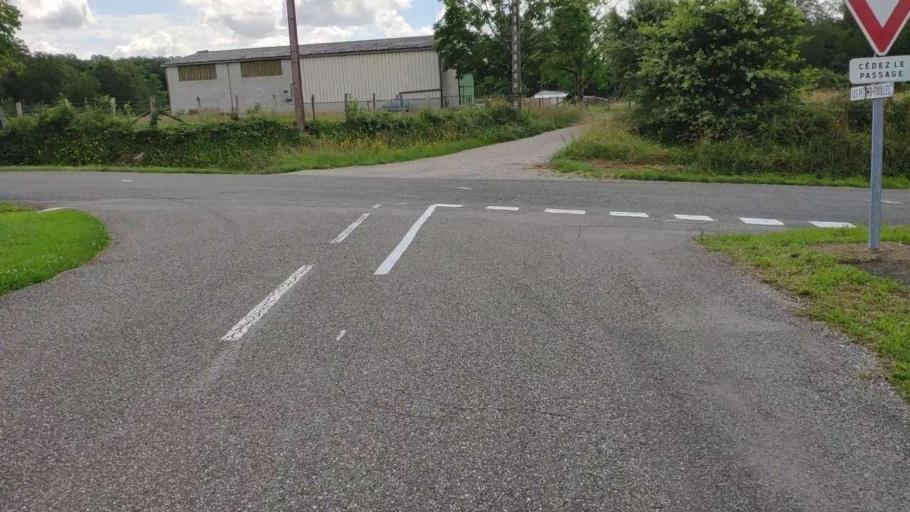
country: FR
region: Franche-Comte
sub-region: Departement du Jura
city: Bletterans
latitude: 46.8453
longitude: 5.4671
